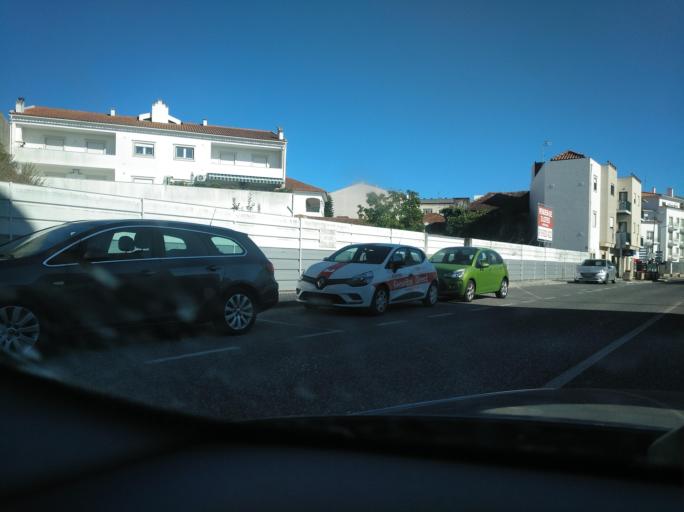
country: PT
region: Leiria
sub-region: Porto de Mos
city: Porto de Mos
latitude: 39.6006
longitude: -8.8202
